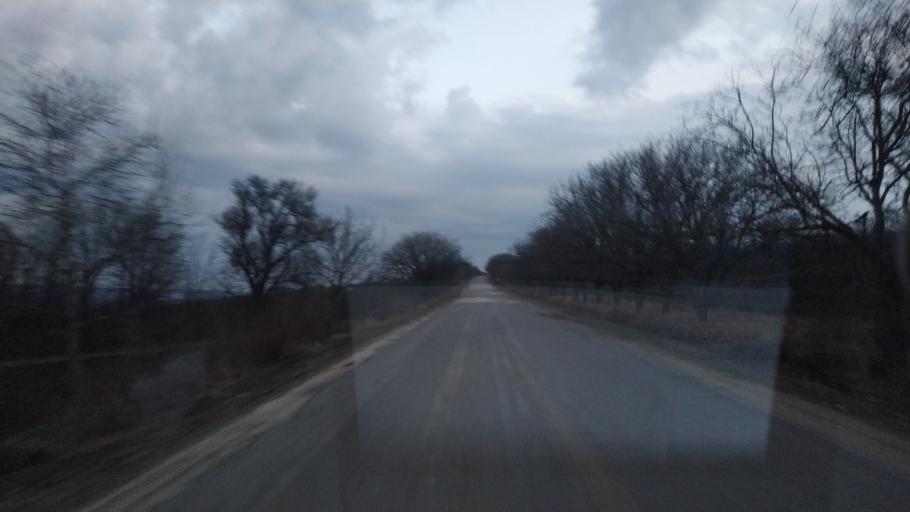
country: MD
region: Anenii Noi
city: Anenii Noi
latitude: 46.9399
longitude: 29.2847
